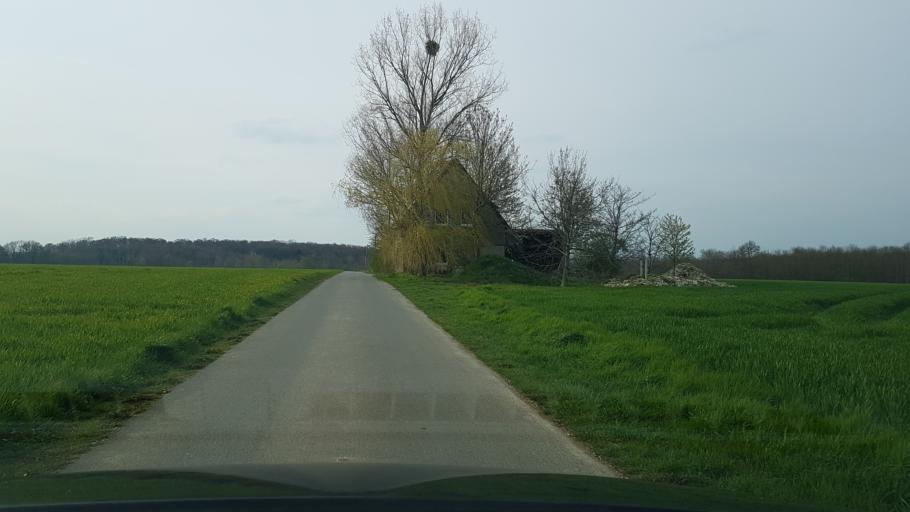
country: DE
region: North Rhine-Westphalia
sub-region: Regierungsbezirk Detmold
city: Paderborn
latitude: 51.6353
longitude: 8.7271
